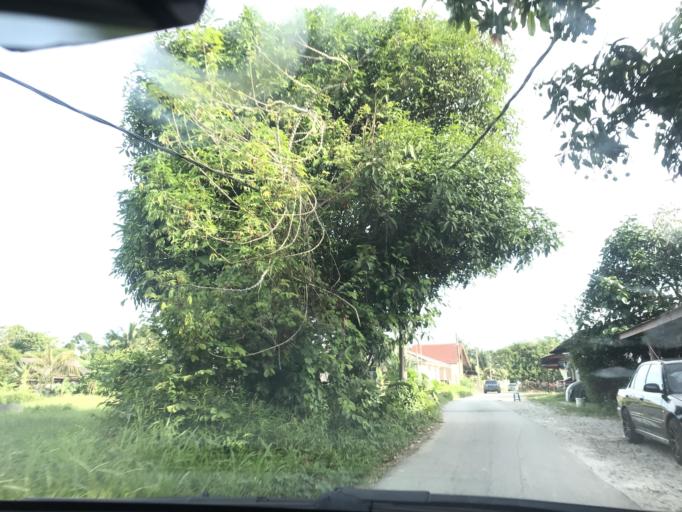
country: MY
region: Kelantan
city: Kota Bharu
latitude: 6.1337
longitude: 102.2229
